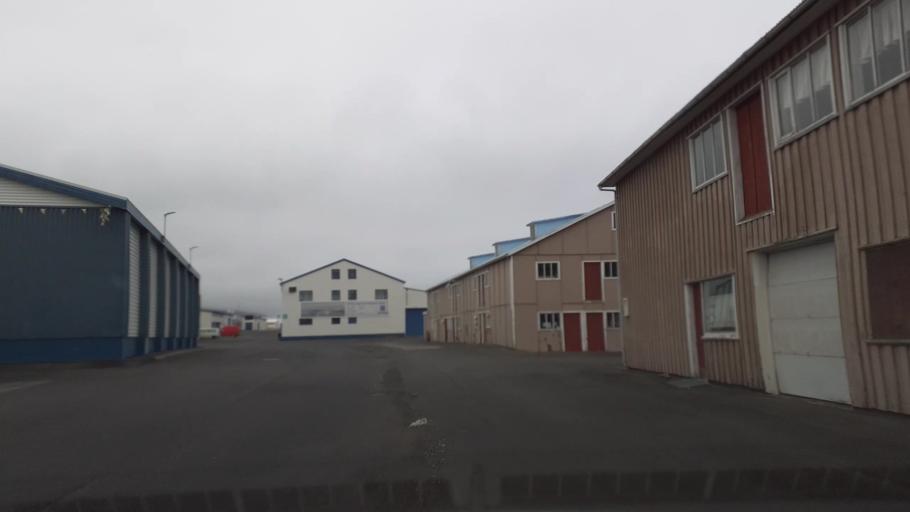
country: IS
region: Northeast
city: Dalvik
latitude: 65.9737
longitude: -18.5293
